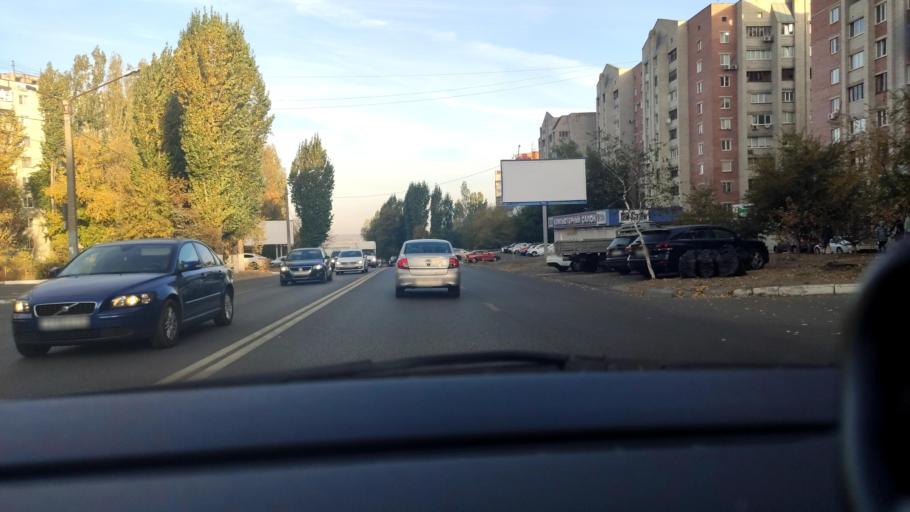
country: RU
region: Voronezj
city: Podgornoye
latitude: 51.7076
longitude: 39.1422
